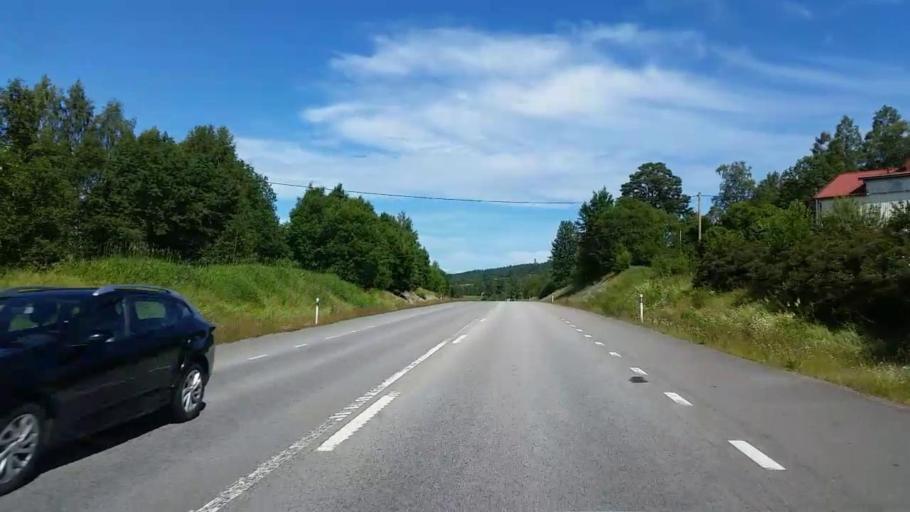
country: SE
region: Dalarna
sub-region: Rattviks Kommun
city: Raettvik
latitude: 60.8435
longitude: 15.1029
